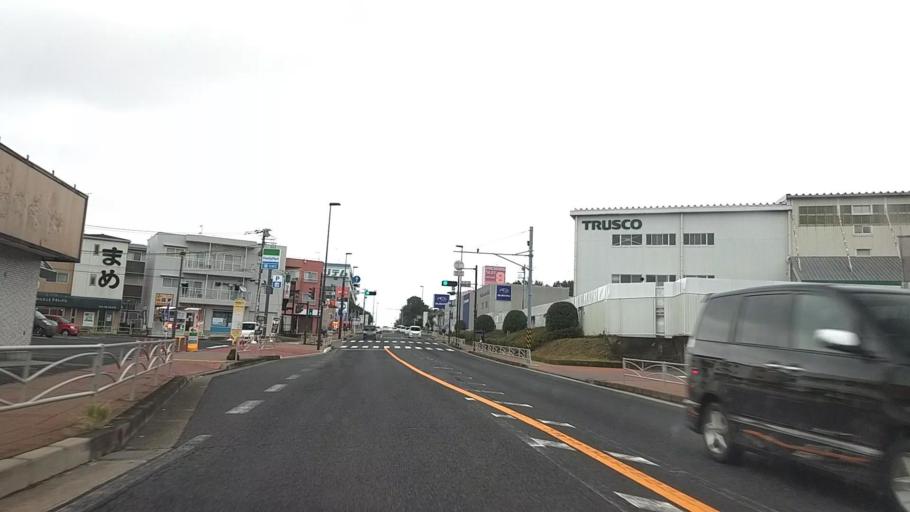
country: JP
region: Kanagawa
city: Isehara
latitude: 35.4122
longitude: 139.3325
